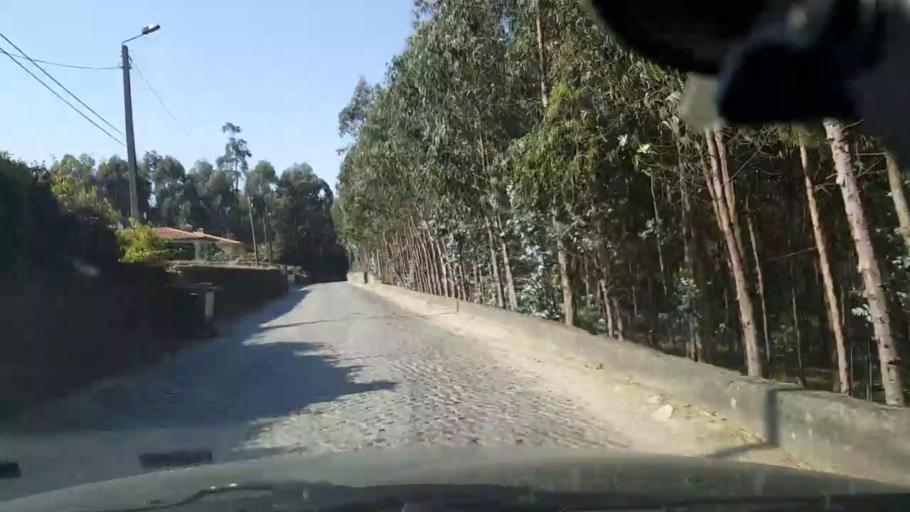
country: PT
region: Porto
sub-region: Vila do Conde
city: Arvore
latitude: 41.3831
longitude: -8.6841
